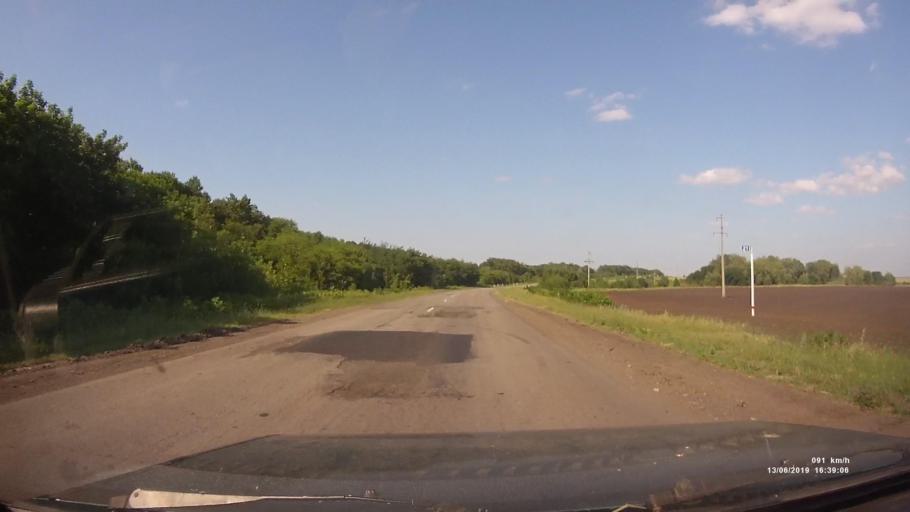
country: RU
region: Rostov
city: Kazanskaya
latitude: 49.9257
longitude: 41.3346
